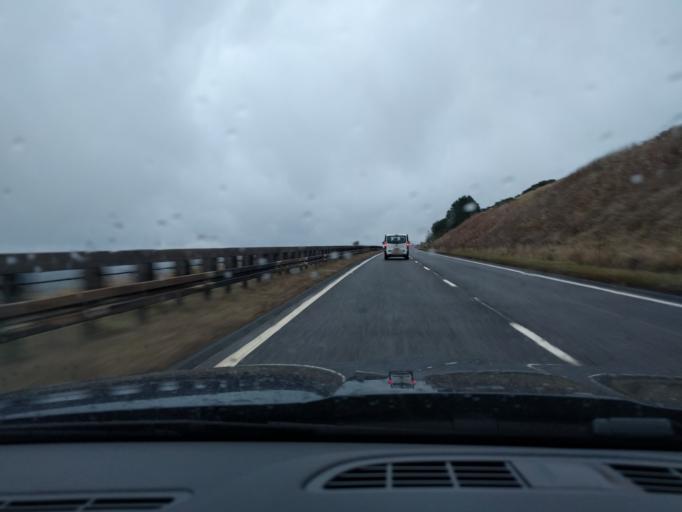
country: GB
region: Scotland
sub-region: The Scottish Borders
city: Eyemouth
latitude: 55.8342
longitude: -2.0633
